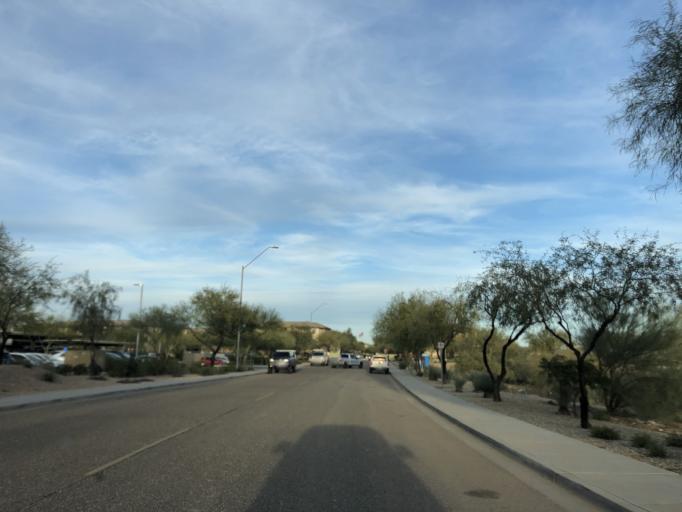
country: US
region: Arizona
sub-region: Maricopa County
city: Anthem
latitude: 33.7036
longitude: -112.1136
